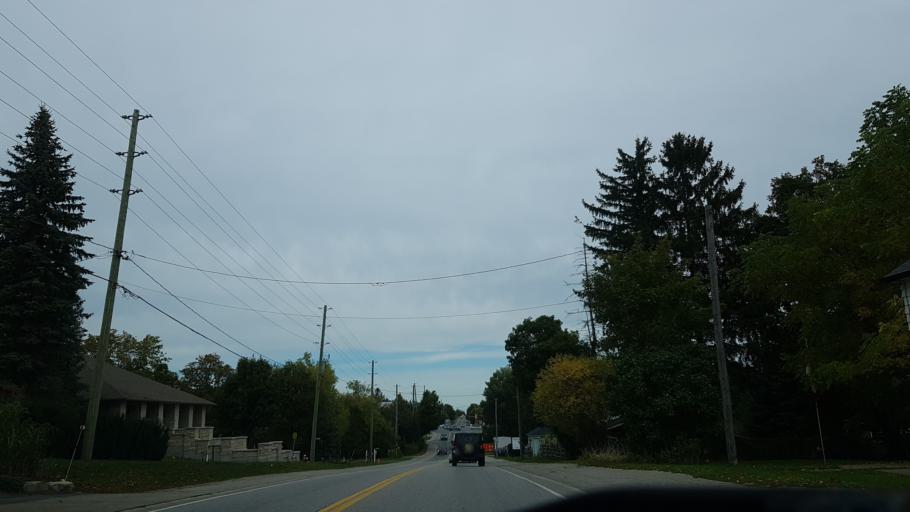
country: CA
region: Ontario
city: Orangeville
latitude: 43.8579
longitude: -79.9985
